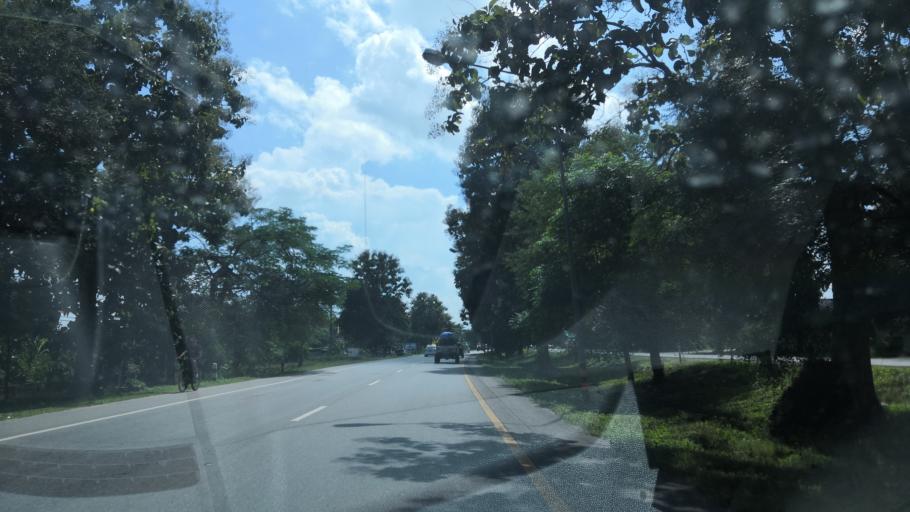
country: TH
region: Chiang Rai
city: Mae Lao
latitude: 19.7622
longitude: 99.7350
